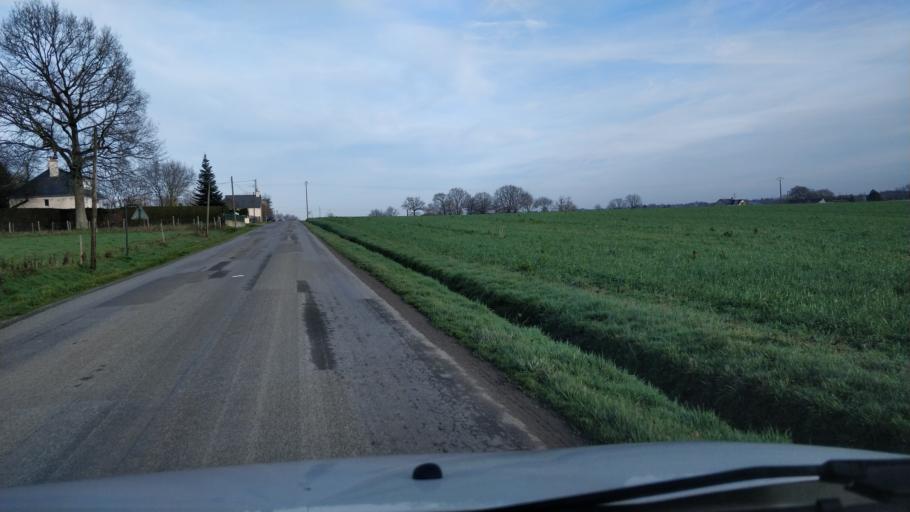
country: FR
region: Brittany
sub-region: Departement d'Ille-et-Vilaine
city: Argentre-du-Plessis
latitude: 48.0335
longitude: -1.1670
